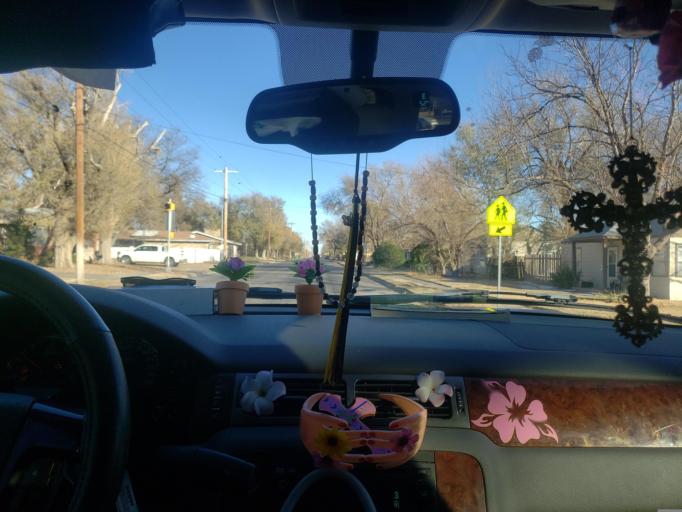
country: US
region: Kansas
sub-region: Finney County
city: Garden City
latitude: 37.9677
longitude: -100.8601
